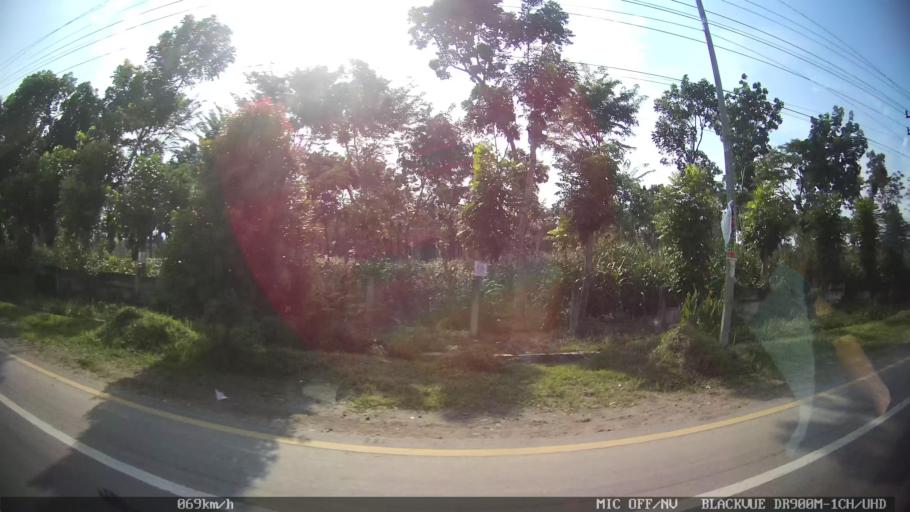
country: ID
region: North Sumatra
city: Percut
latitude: 3.5859
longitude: 98.8038
